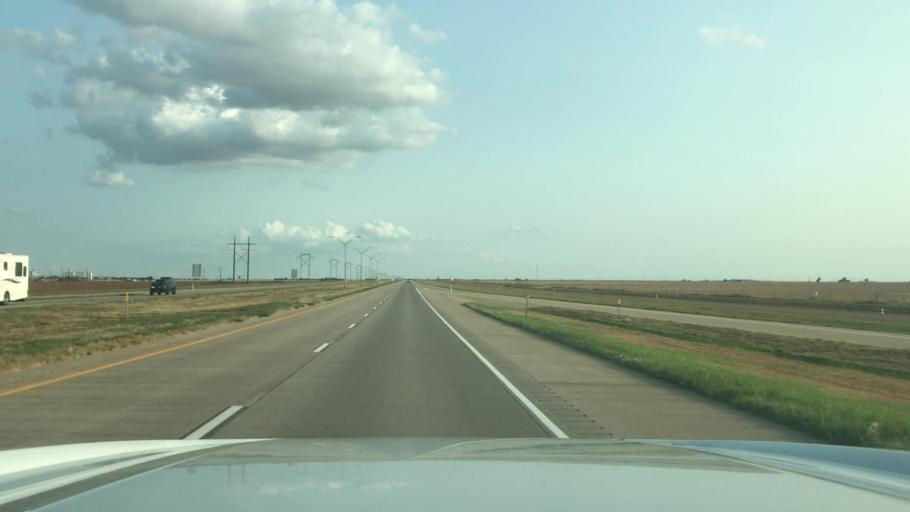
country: US
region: Texas
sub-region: Swisher County
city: Tulia
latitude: 34.5689
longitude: -101.7950
